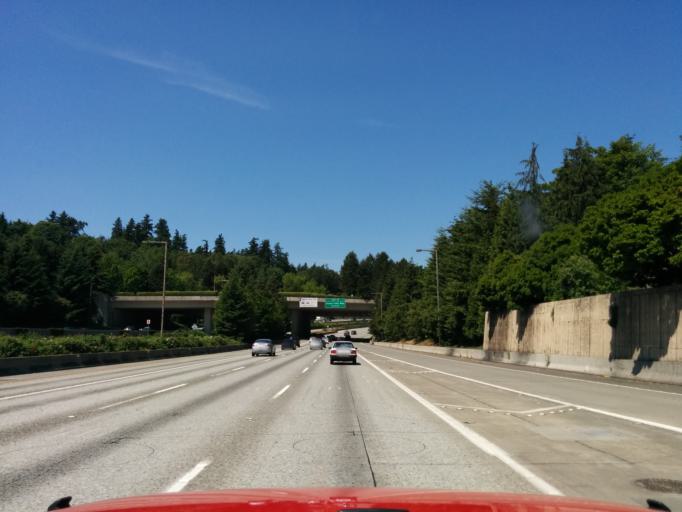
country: US
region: Washington
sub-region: King County
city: Mercer Island
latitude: 47.5787
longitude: -122.2100
